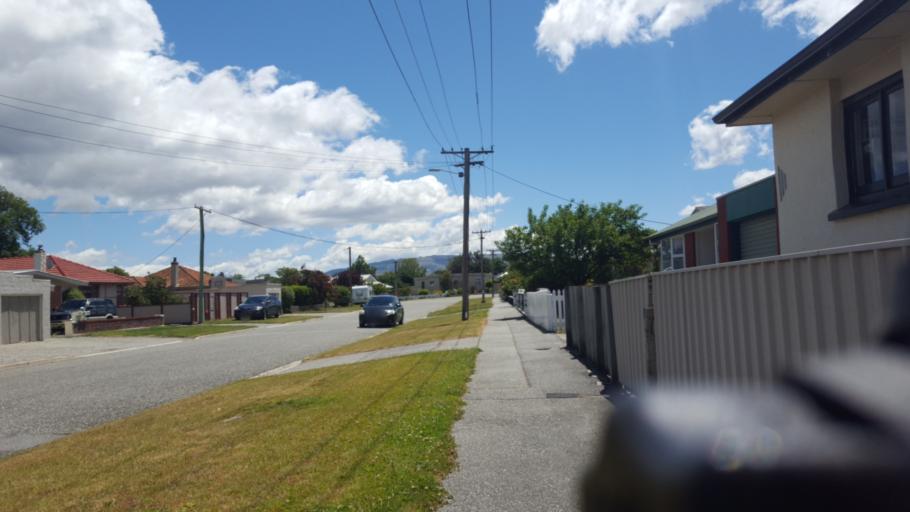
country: NZ
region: Otago
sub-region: Queenstown-Lakes District
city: Wanaka
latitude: -45.2507
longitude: 169.3950
